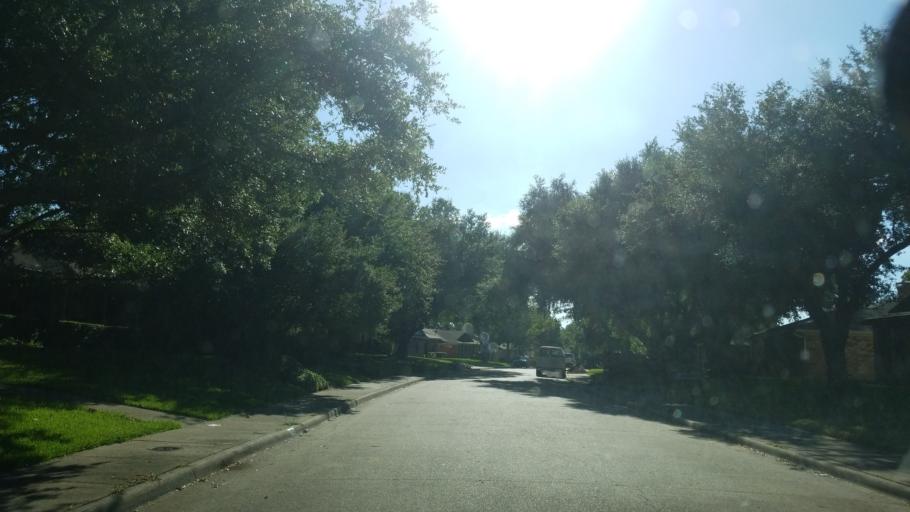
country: US
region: Texas
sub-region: Dallas County
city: Balch Springs
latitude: 32.7872
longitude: -96.7028
